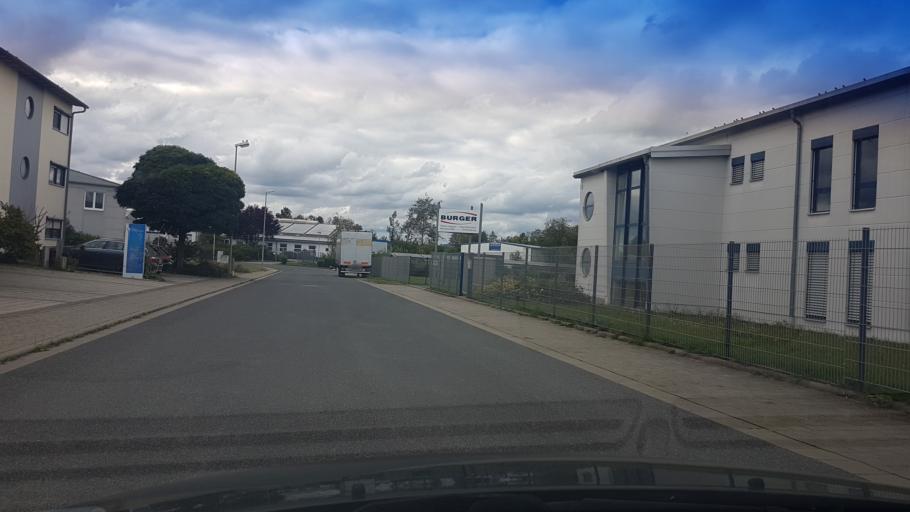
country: DE
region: Bavaria
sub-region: Upper Franconia
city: Breitengussbach
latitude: 49.9754
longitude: 10.8831
